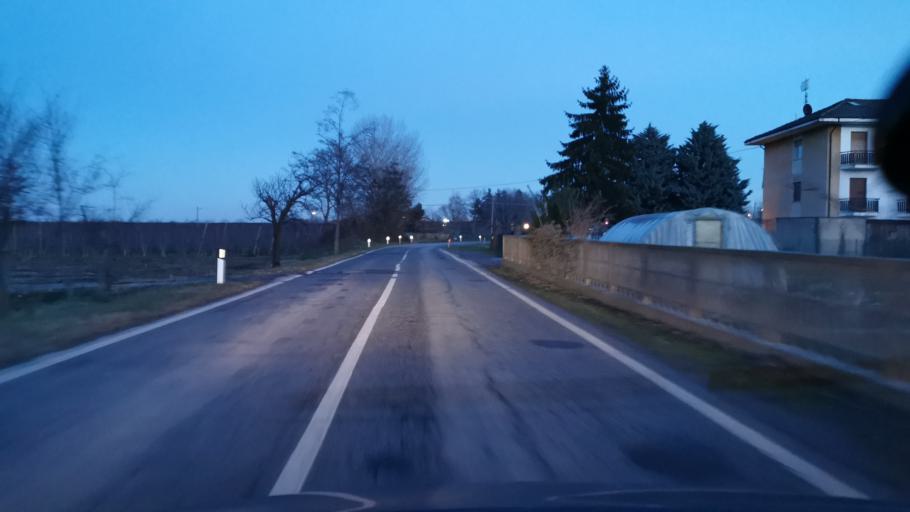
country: IT
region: Piedmont
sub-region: Provincia di Cuneo
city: Roata Rossi
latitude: 44.4421
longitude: 7.5609
